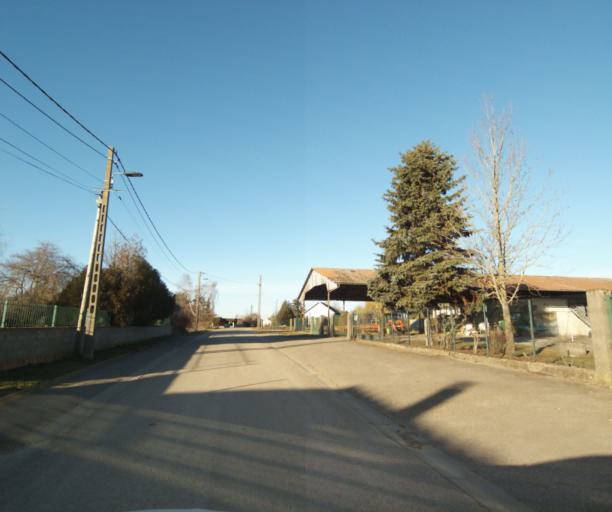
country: FR
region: Lorraine
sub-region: Departement de Meurthe-et-Moselle
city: Laneuveville-devant-Nancy
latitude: 48.6430
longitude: 6.2332
